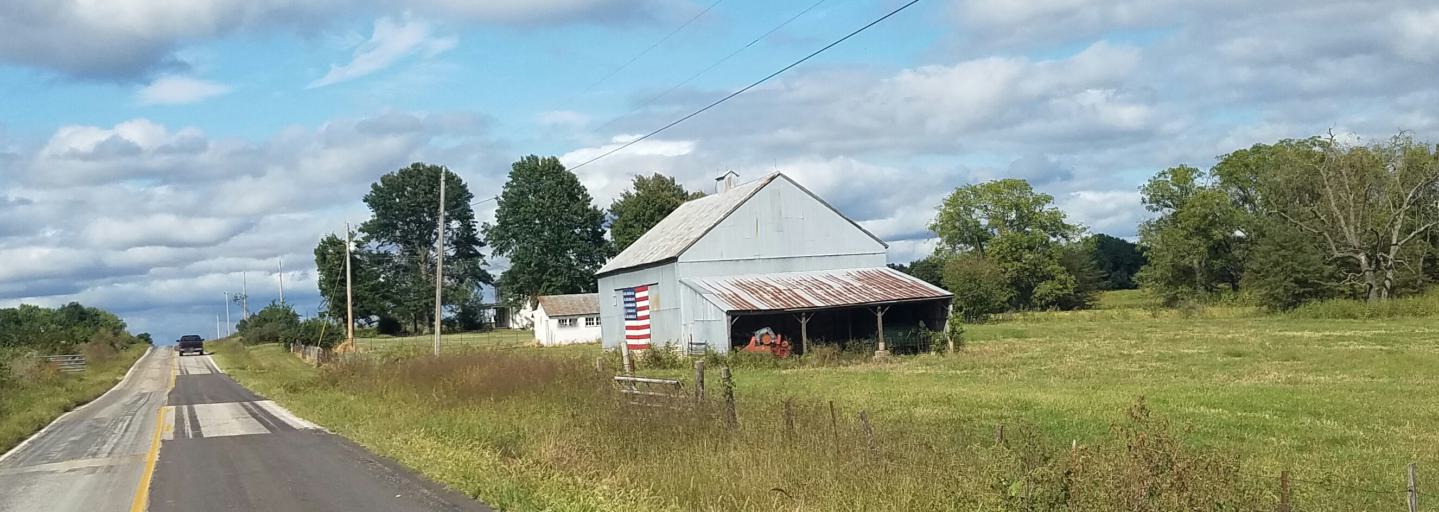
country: US
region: Missouri
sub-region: Moniteau County
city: California
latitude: 38.6750
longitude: -92.5863
